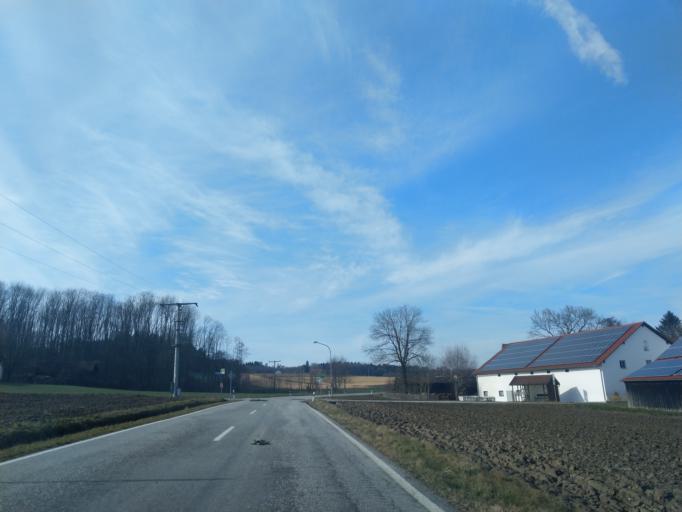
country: DE
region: Bavaria
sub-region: Lower Bavaria
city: Buchhofen
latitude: 48.6684
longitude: 12.9298
